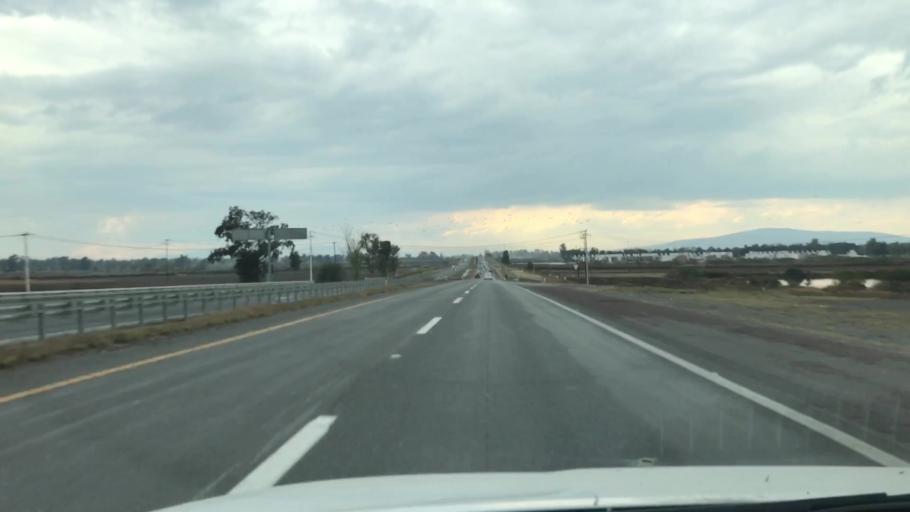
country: MX
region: Guanajuato
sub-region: Irapuato
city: Cuarta Brigada
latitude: 20.6540
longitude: -101.3007
